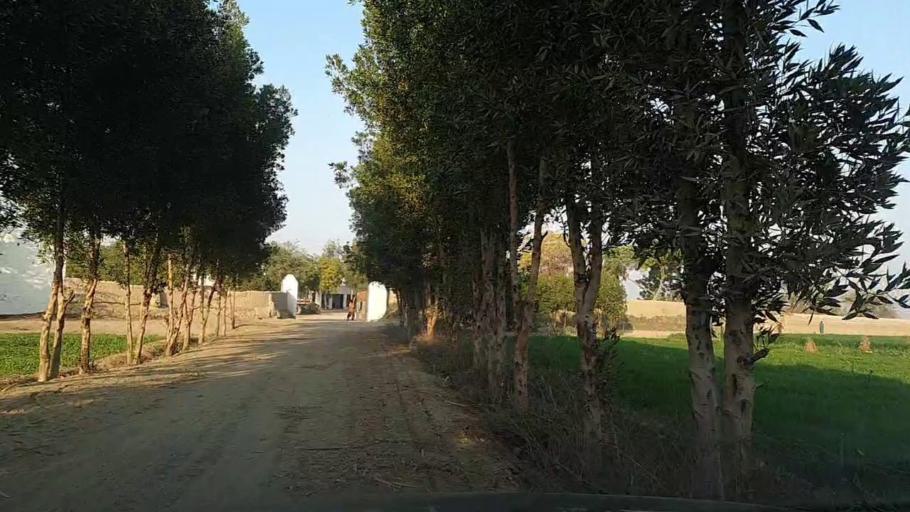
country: PK
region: Sindh
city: Daur
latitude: 26.4668
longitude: 68.3882
